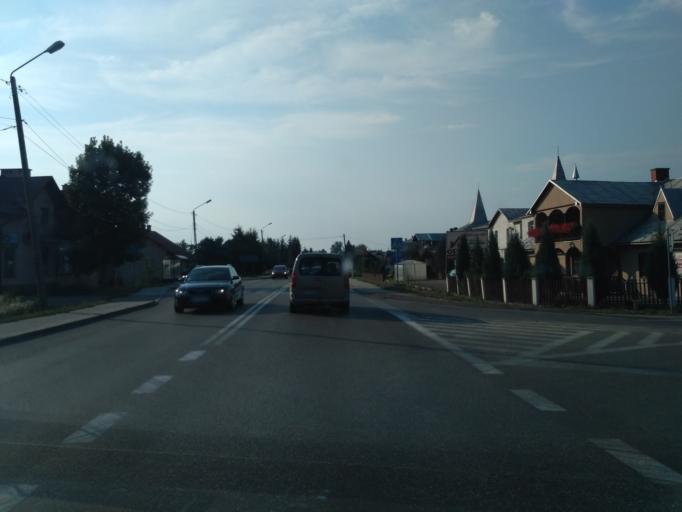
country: PL
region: Subcarpathian Voivodeship
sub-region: Powiat brzozowski
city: Grabownica Starzenska
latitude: 49.6583
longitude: 22.0777
